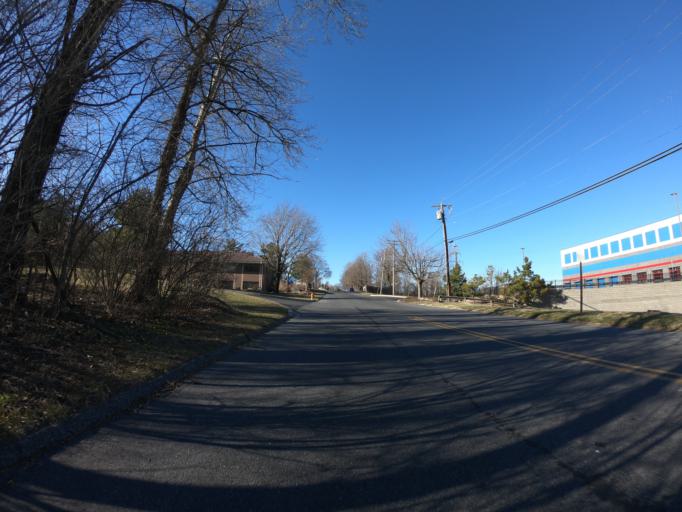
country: US
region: Maryland
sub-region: Howard County
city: Ellicott City
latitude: 39.2742
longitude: -76.8223
